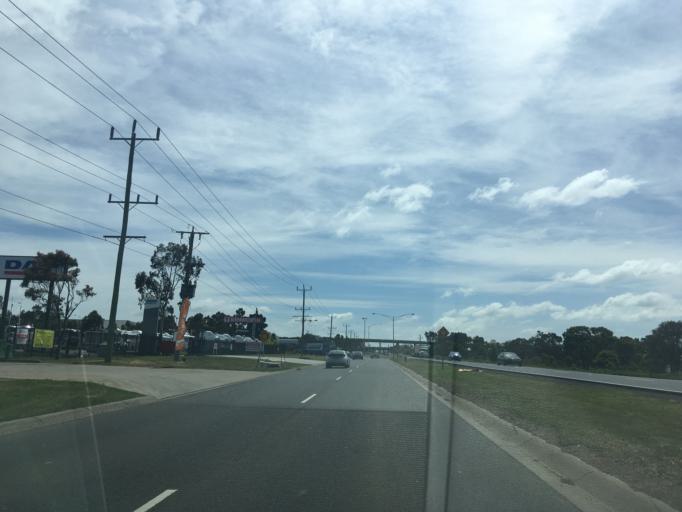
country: AU
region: Victoria
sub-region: Brimbank
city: Derrimut
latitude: -37.8073
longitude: 144.7881
